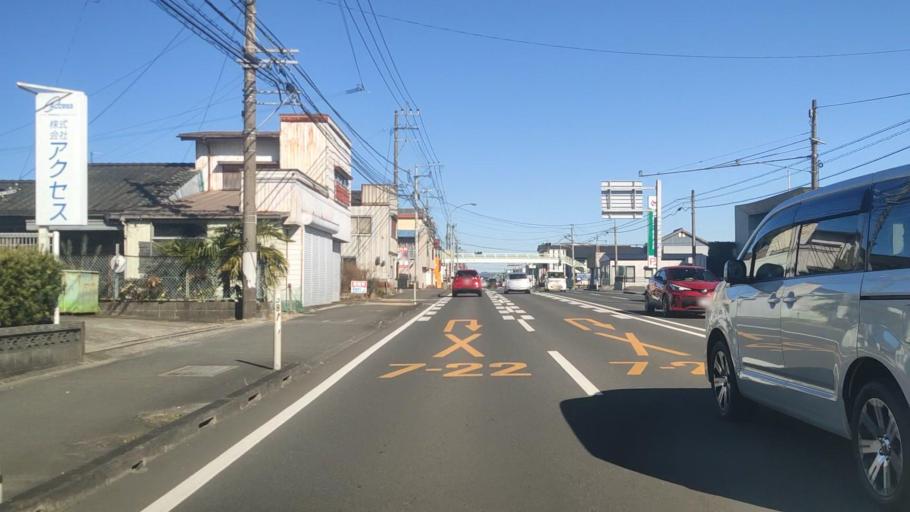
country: JP
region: Miyazaki
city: Miyakonojo
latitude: 31.7413
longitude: 131.0728
